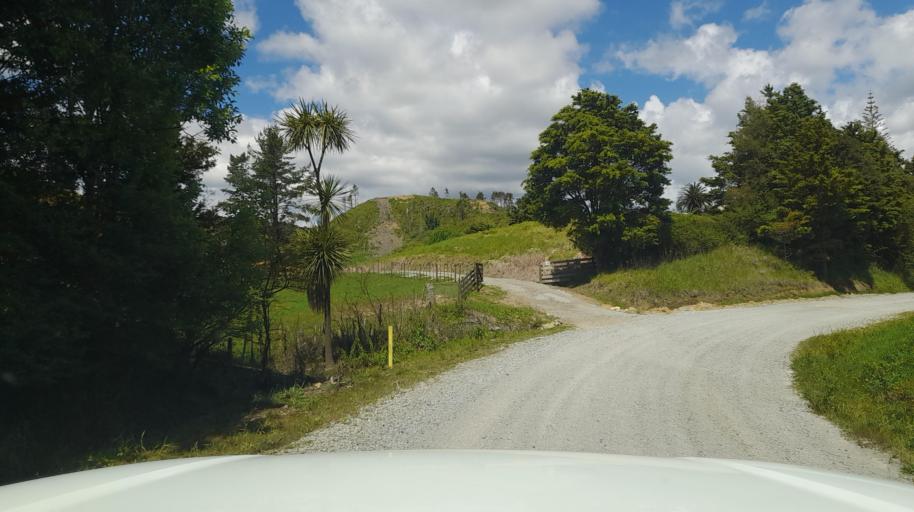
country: NZ
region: Northland
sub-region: Far North District
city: Taipa
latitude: -35.1207
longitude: 173.4065
